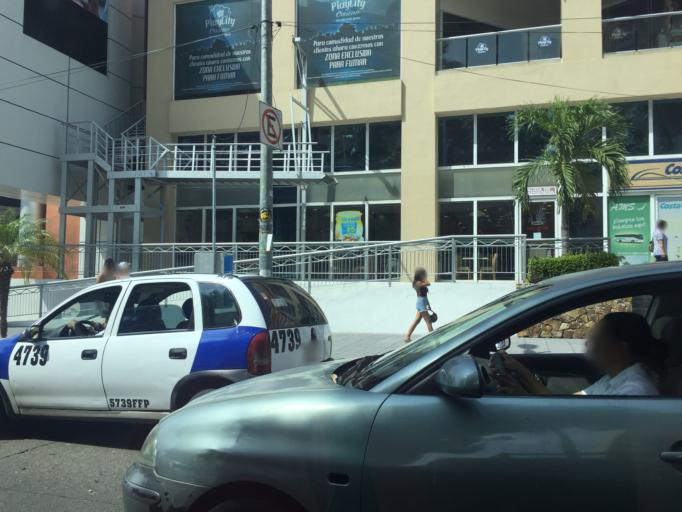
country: MX
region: Guerrero
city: Acapulco de Juarez
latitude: 16.8608
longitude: -99.8825
